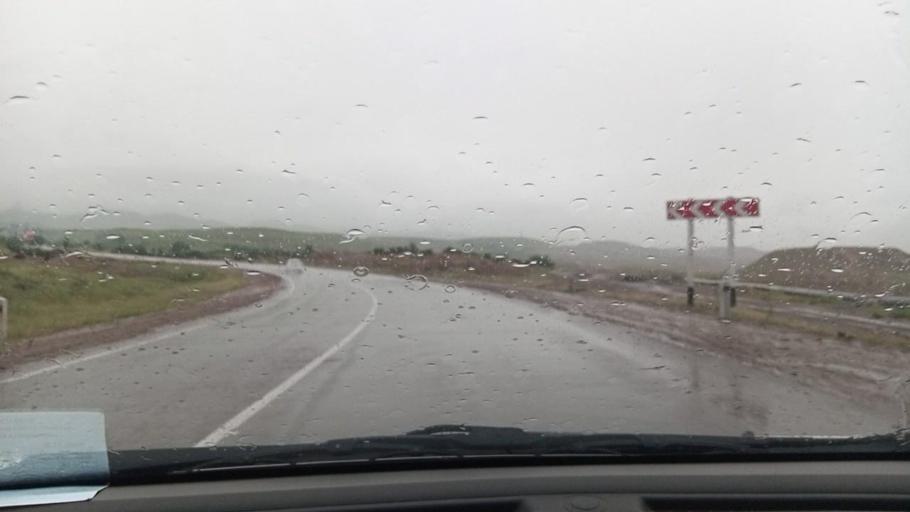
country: UZ
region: Toshkent
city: Angren
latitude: 41.0455
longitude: 70.1580
